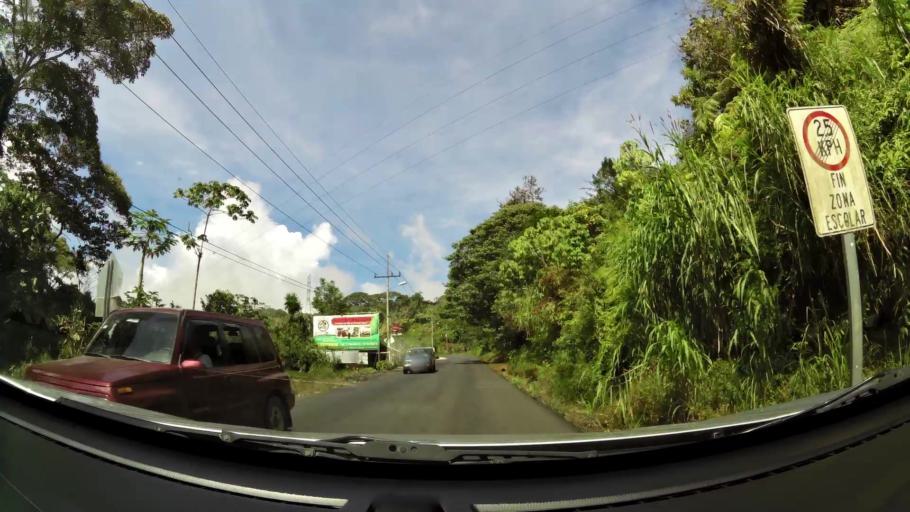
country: CR
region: San Jose
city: San Isidro
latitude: 9.3264
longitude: -83.7465
